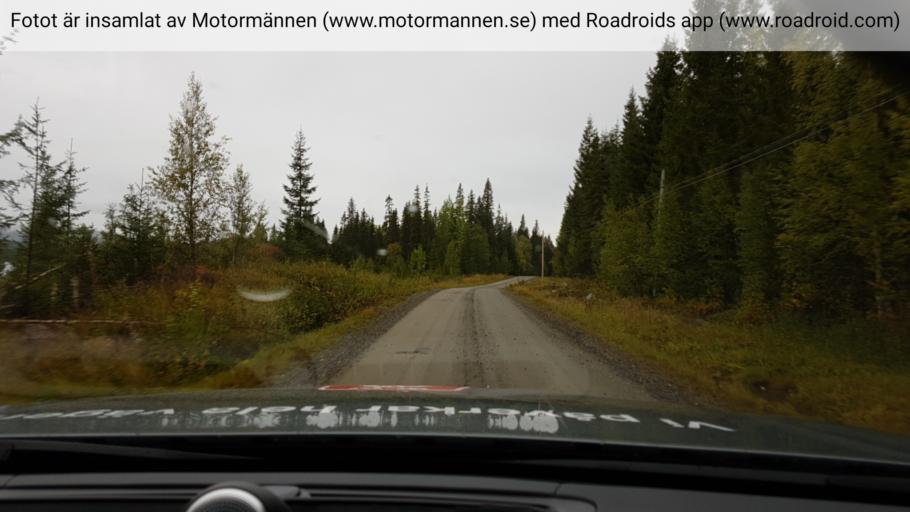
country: NO
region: Nord-Trondelag
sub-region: Lierne
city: Sandvika
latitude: 64.4659
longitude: 14.3119
